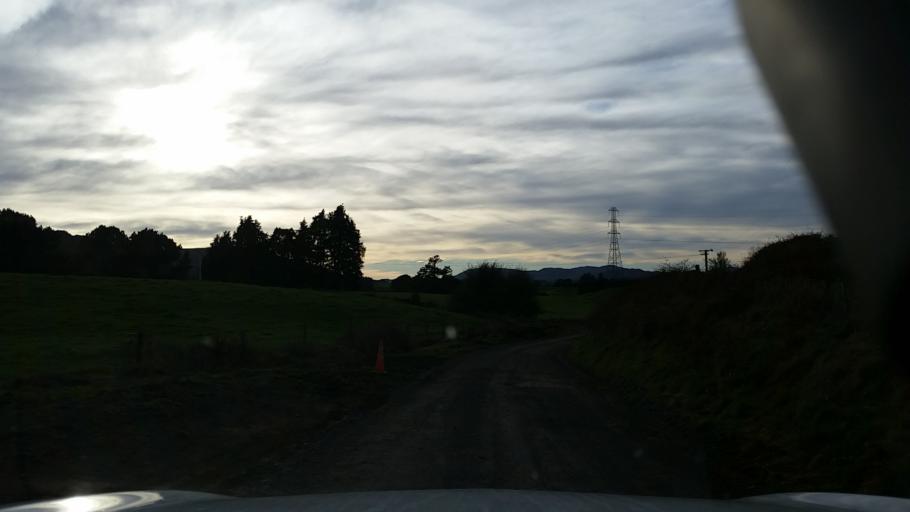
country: NZ
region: Bay of Plenty
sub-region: Rotorua District
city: Rotorua
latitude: -38.2278
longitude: 176.1617
